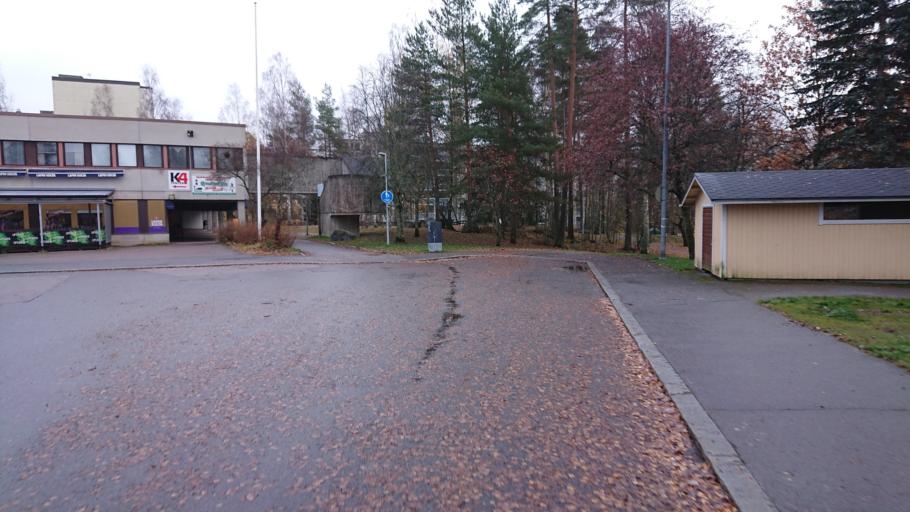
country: FI
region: Pirkanmaa
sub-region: Tampere
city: Tampere
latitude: 61.4521
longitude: 23.8317
